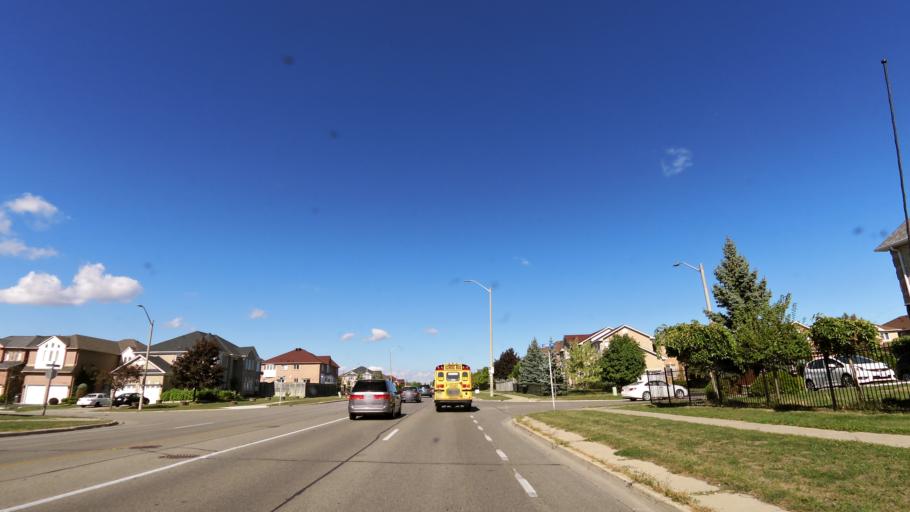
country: CA
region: Ontario
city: Mississauga
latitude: 43.5924
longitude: -79.6884
